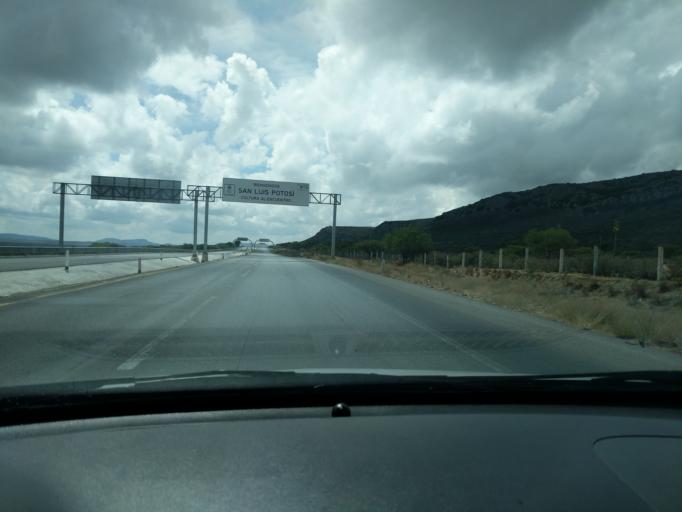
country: MX
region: Zacatecas
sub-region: Pinos
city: Santiago
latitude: 22.4018
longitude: -101.3801
